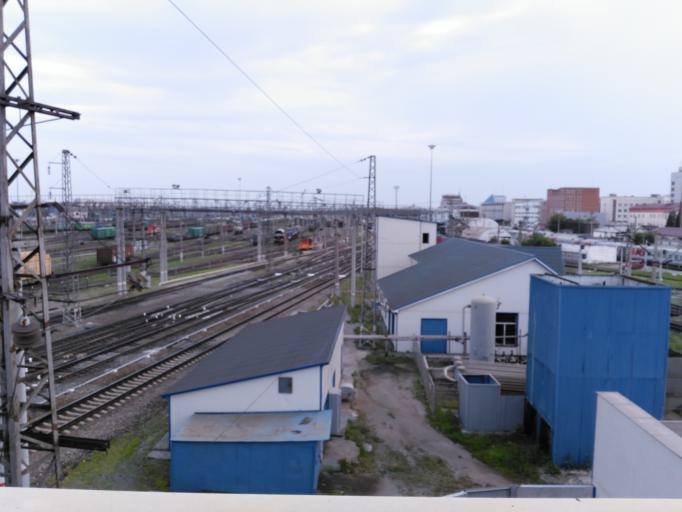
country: RU
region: Chelyabinsk
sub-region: Gorod Chelyabinsk
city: Chelyabinsk
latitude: 55.1463
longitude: 61.4210
